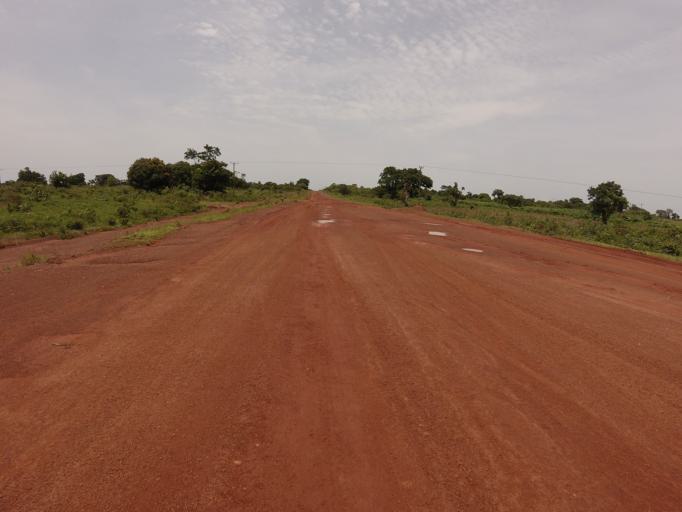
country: GH
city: Kpandae
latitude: 8.7613
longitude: 0.0598
